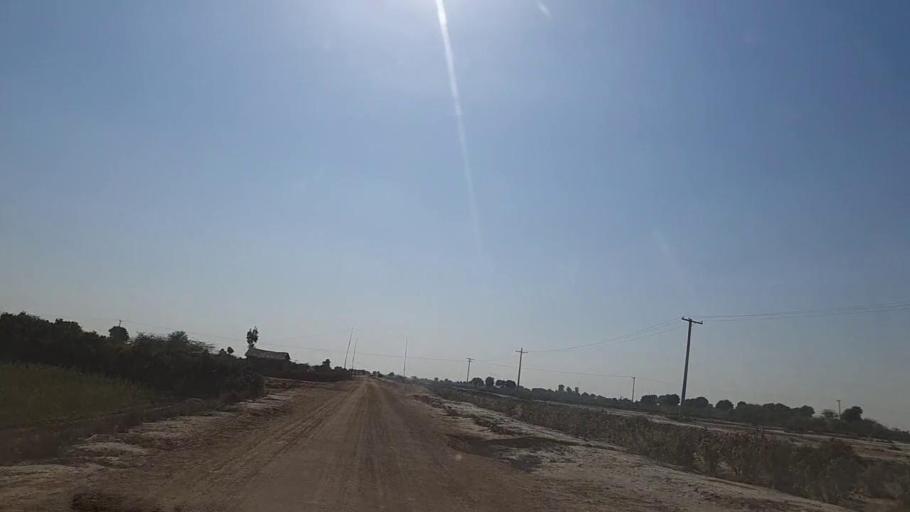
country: PK
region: Sindh
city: Digri
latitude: 25.1261
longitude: 69.0540
